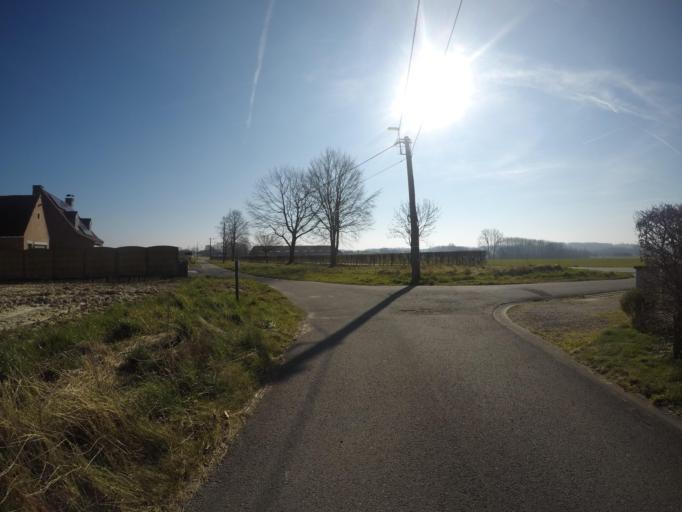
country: BE
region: Flanders
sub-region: Provincie Oost-Vlaanderen
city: Sint-Maria-Lierde
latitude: 50.8012
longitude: 3.7926
